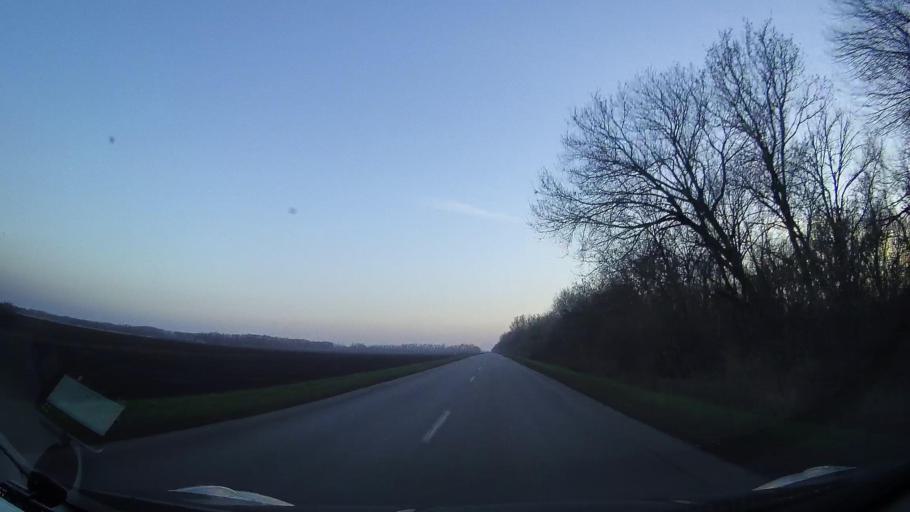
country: RU
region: Rostov
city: Zernograd
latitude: 46.9998
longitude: 40.3915
